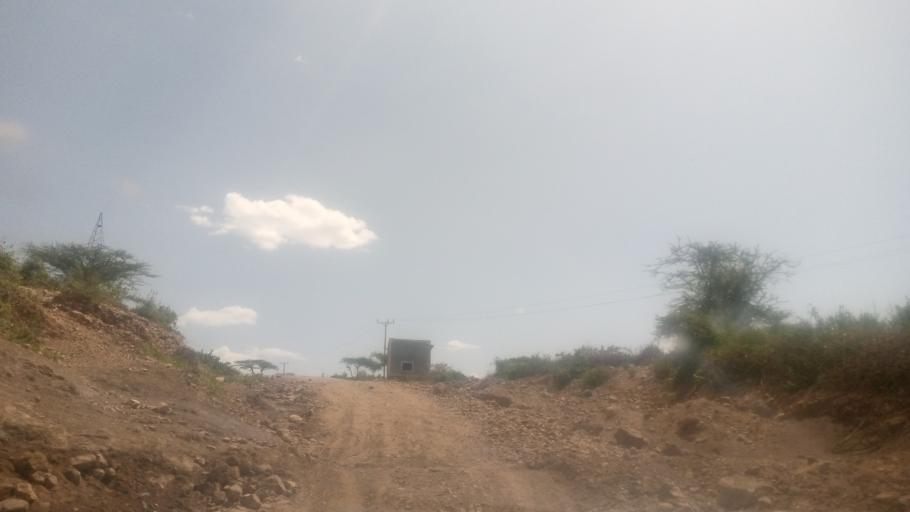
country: ET
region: Oromiya
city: Deder
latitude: 9.5280
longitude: 41.3455
